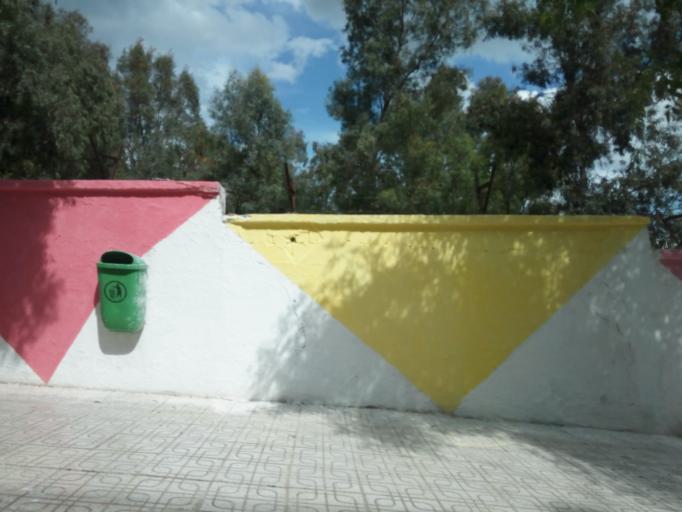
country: DZ
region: Constantine
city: Constantine
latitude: 36.3541
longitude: 6.6093
